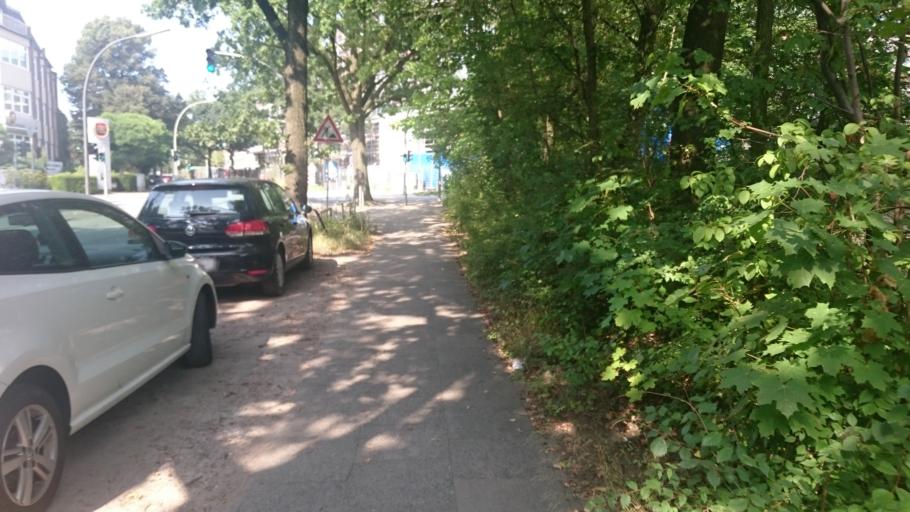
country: DE
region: Hamburg
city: St. Pauli
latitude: 53.5823
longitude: 9.9565
